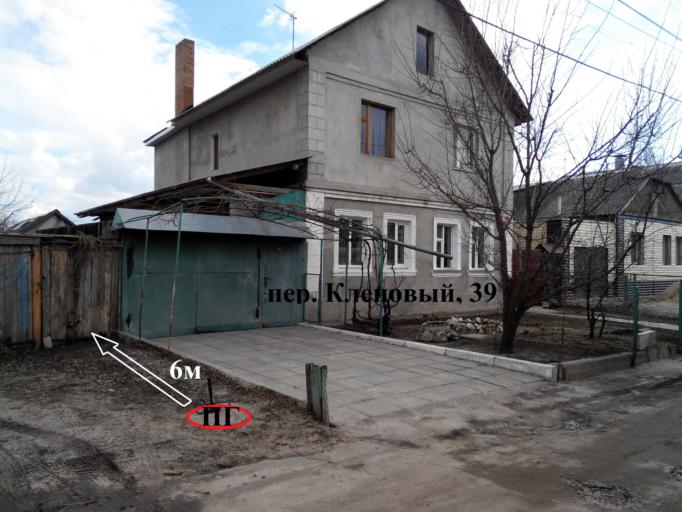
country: RU
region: Voronezj
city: Voronezh
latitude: 51.6336
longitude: 39.1582
